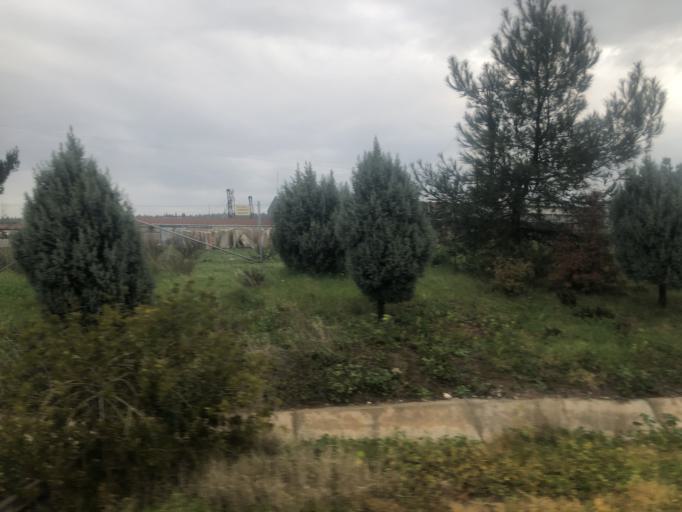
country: TR
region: Izmir
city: Buca
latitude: 38.3670
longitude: 27.2202
